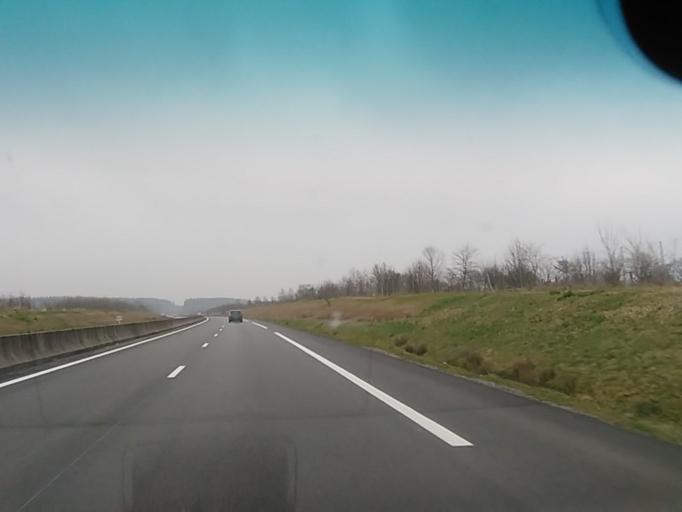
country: FR
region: Lower Normandy
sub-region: Departement de l'Orne
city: Gace
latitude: 48.8037
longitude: 0.3433
